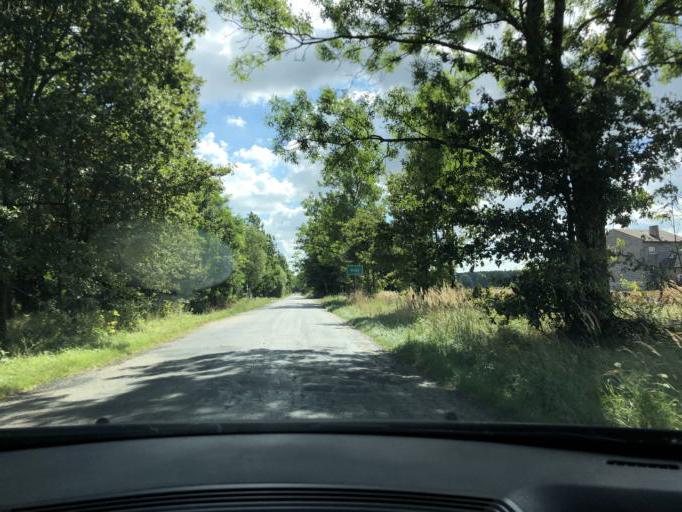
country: PL
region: Lodz Voivodeship
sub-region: Powiat wieruszowski
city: Czastary
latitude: 51.2319
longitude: 18.3537
